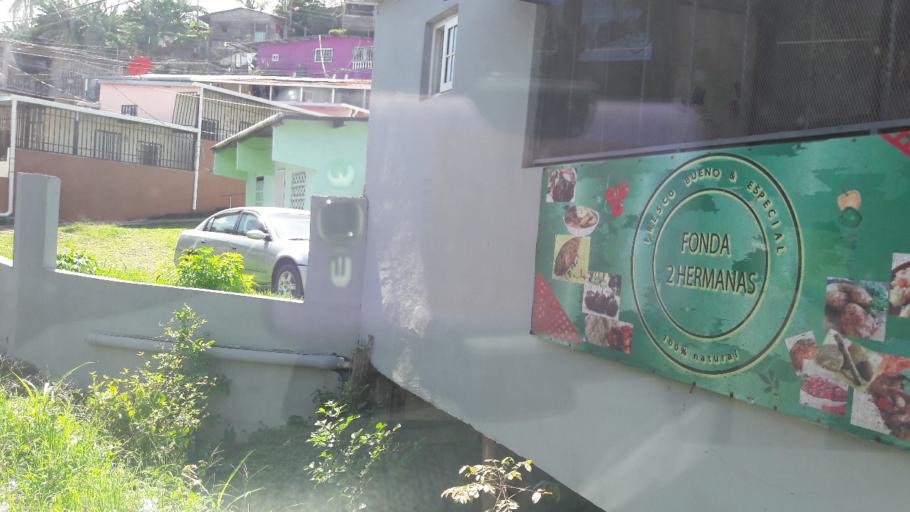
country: PA
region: Panama
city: San Miguelito
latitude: 9.0456
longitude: -79.5056
